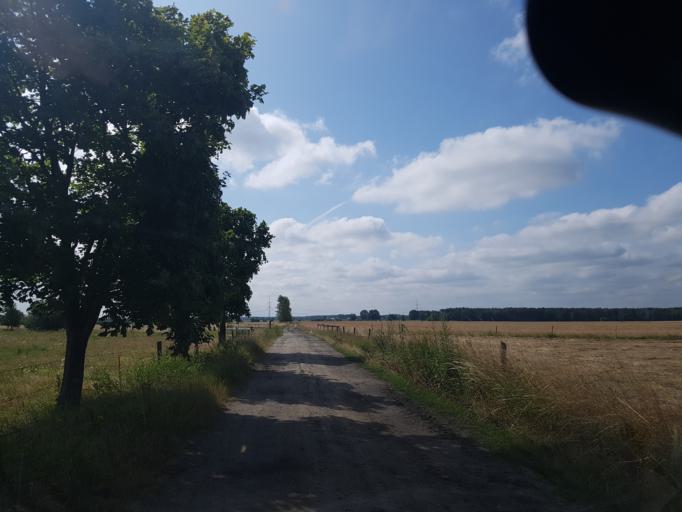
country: DE
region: Brandenburg
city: Schonborn
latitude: 51.5895
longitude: 13.5108
